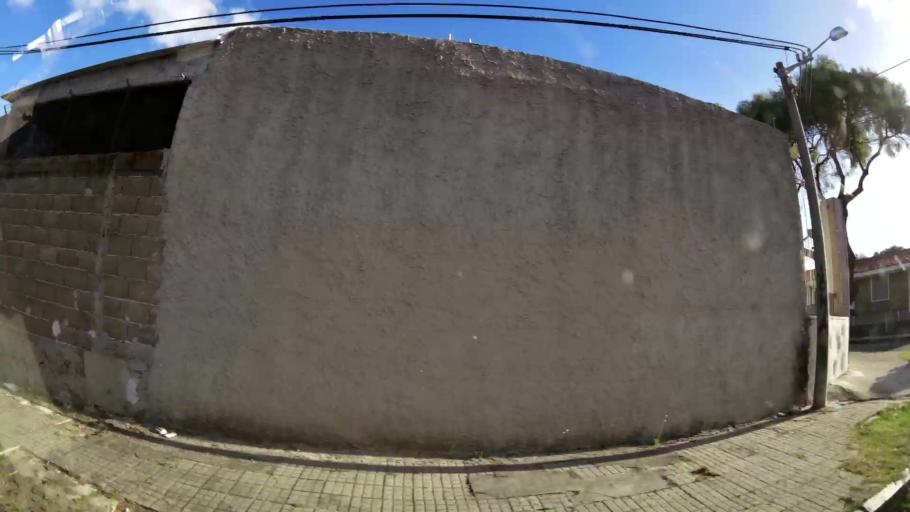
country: UY
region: Montevideo
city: Montevideo
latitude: -34.8741
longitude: -56.2534
